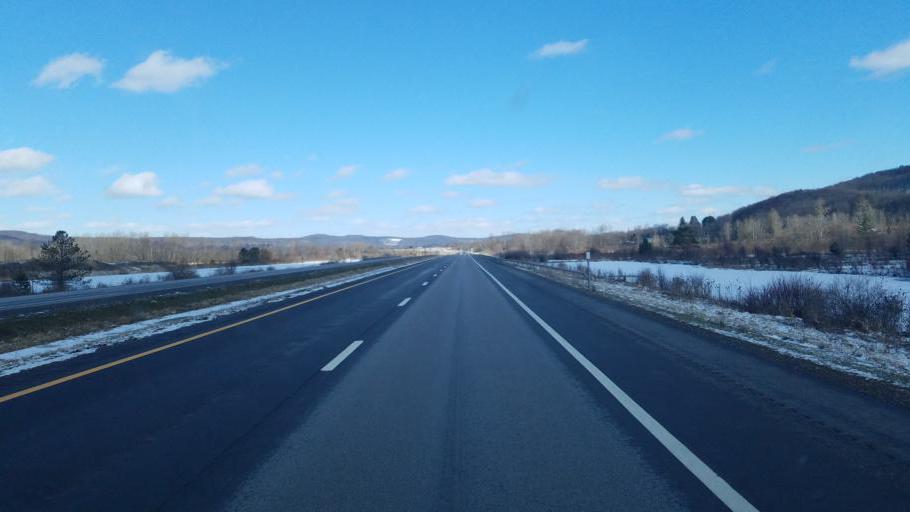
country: US
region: New York
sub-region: Cattaraugus County
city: Allegany
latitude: 42.0902
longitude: -78.5592
